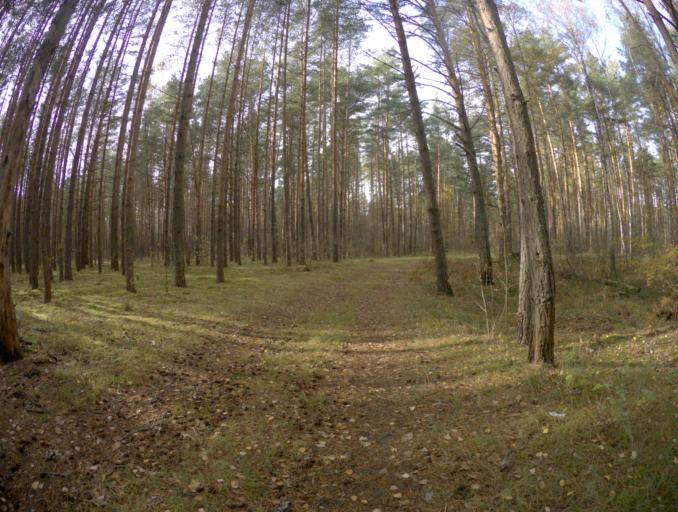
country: RU
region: Vladimir
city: Kommunar
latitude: 56.1187
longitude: 40.4684
